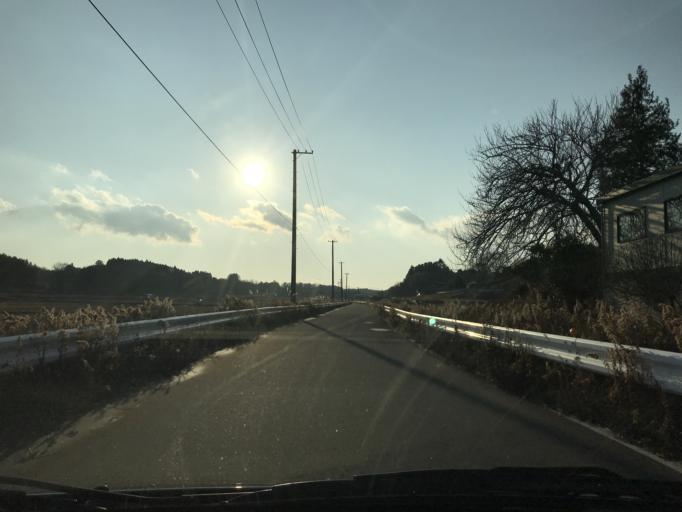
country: JP
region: Miyagi
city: Wakuya
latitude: 38.7037
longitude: 141.1221
